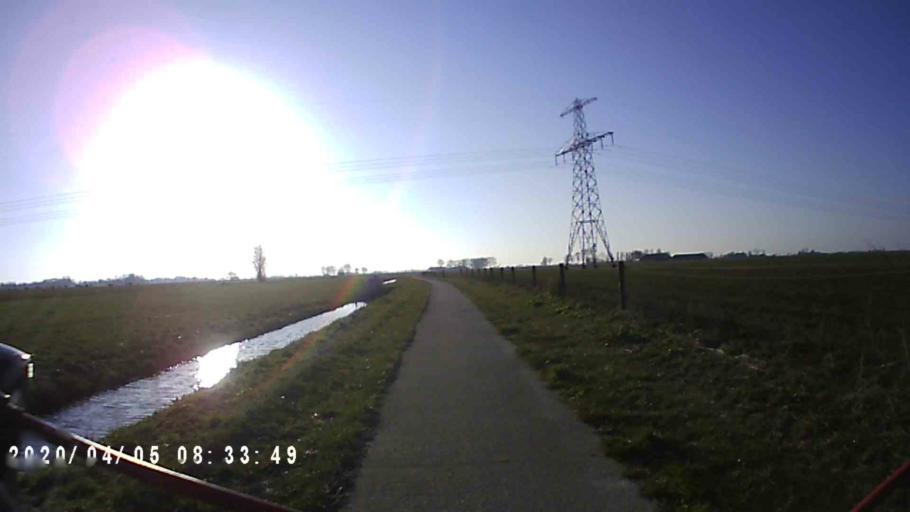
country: NL
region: Groningen
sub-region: Gemeente Winsum
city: Winsum
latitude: 53.3248
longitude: 6.4924
